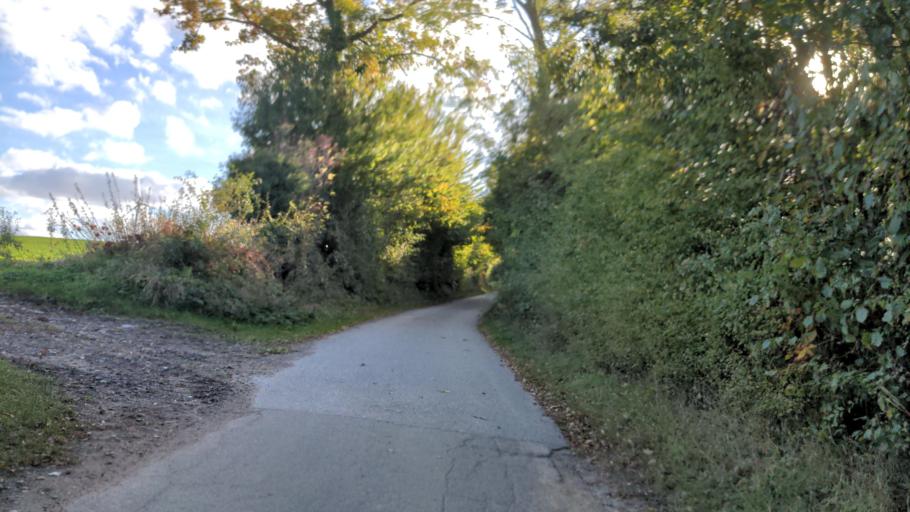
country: DE
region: Schleswig-Holstein
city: Schashagen
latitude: 54.1539
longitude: 10.9145
